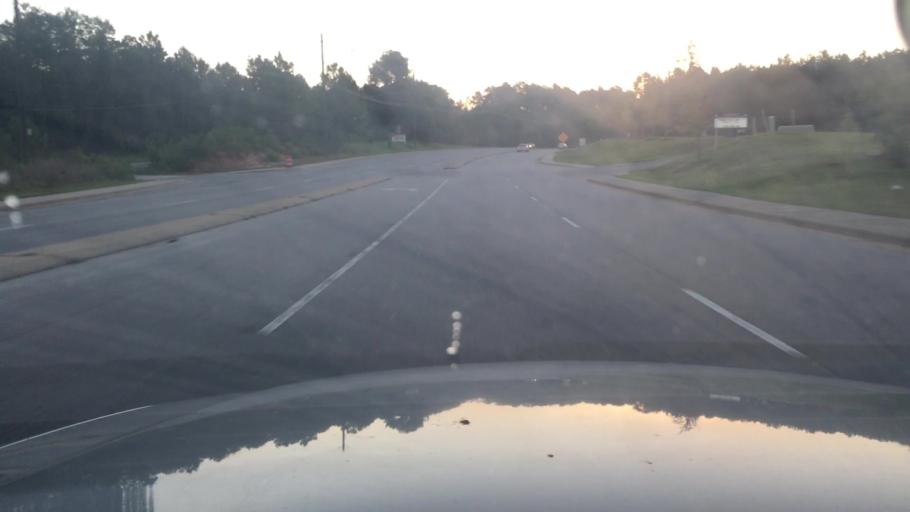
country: US
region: North Carolina
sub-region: Hoke County
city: Rockfish
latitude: 35.0638
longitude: -79.0378
